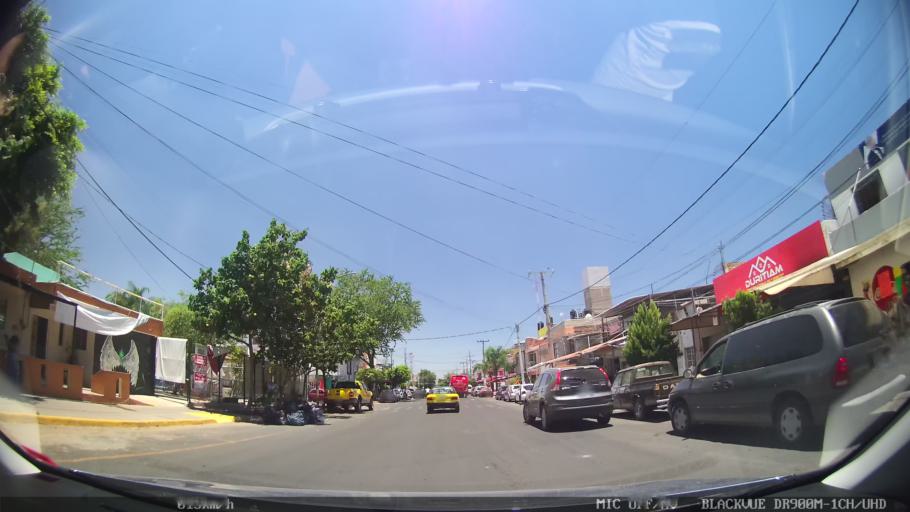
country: MX
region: Jalisco
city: Tlaquepaque
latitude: 20.6726
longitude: -103.2867
